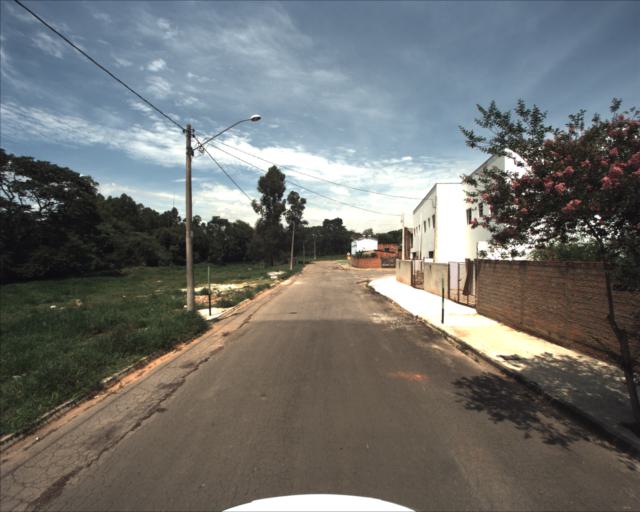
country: BR
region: Sao Paulo
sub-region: Sorocaba
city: Sorocaba
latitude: -23.4127
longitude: -47.4053
